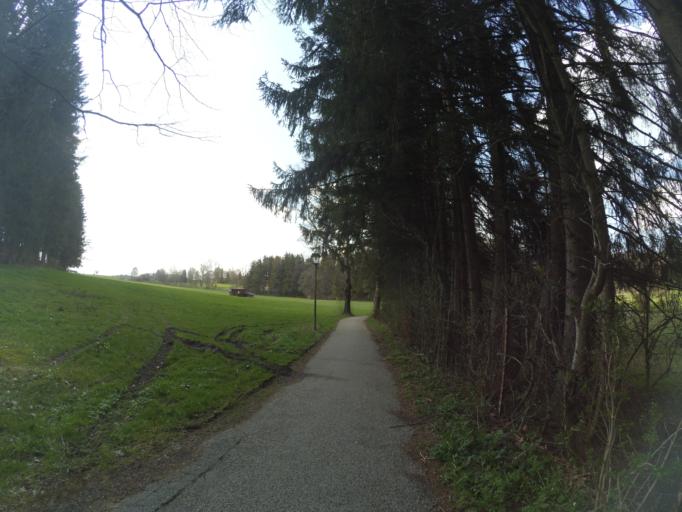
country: DE
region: Bavaria
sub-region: Swabia
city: Bad Worishofen
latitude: 48.0056
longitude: 10.5763
